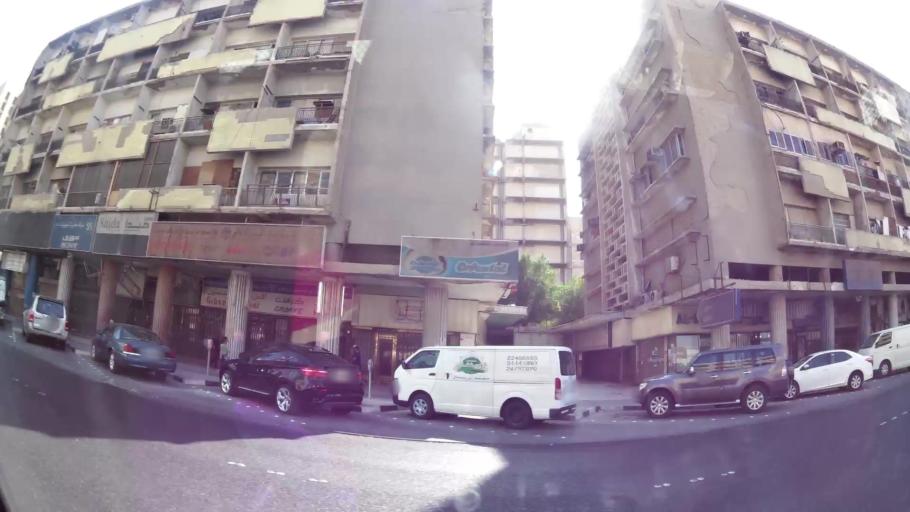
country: KW
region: Al Asimah
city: Kuwait City
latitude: 29.3651
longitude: 47.9660
